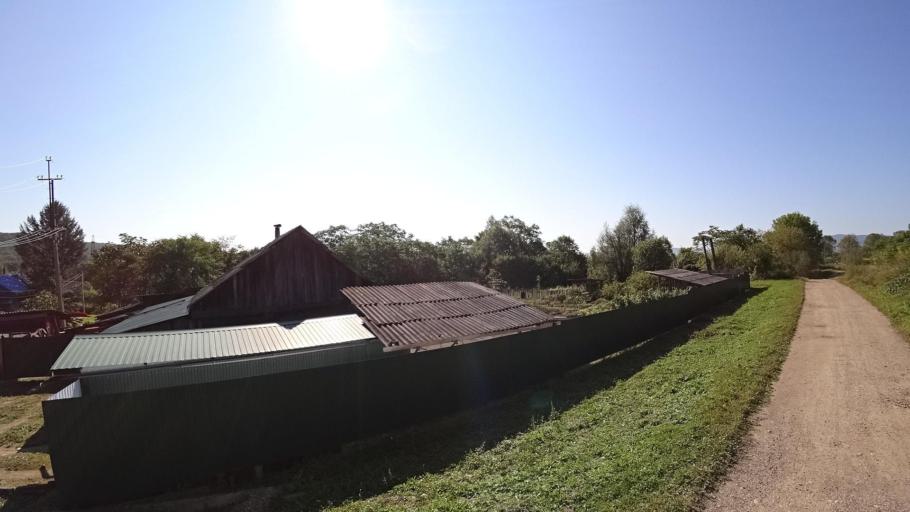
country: RU
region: Jewish Autonomous Oblast
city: Bira
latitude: 49.0063
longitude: 132.4745
